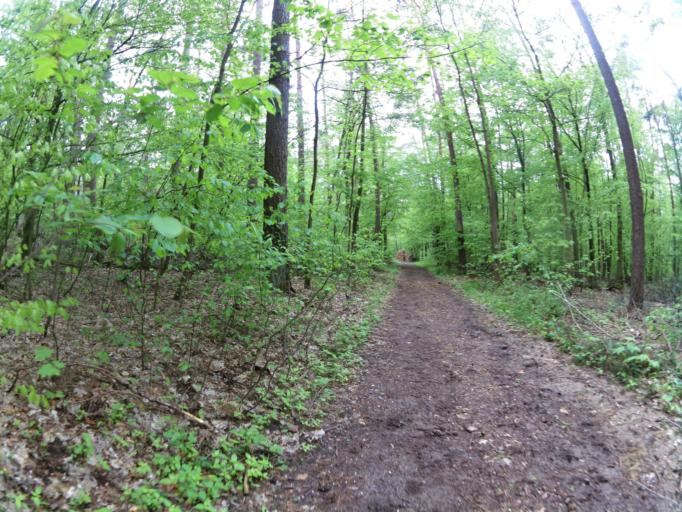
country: DE
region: Bavaria
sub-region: Regierungsbezirk Unterfranken
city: Sommerhausen
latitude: 49.7049
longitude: 10.0440
